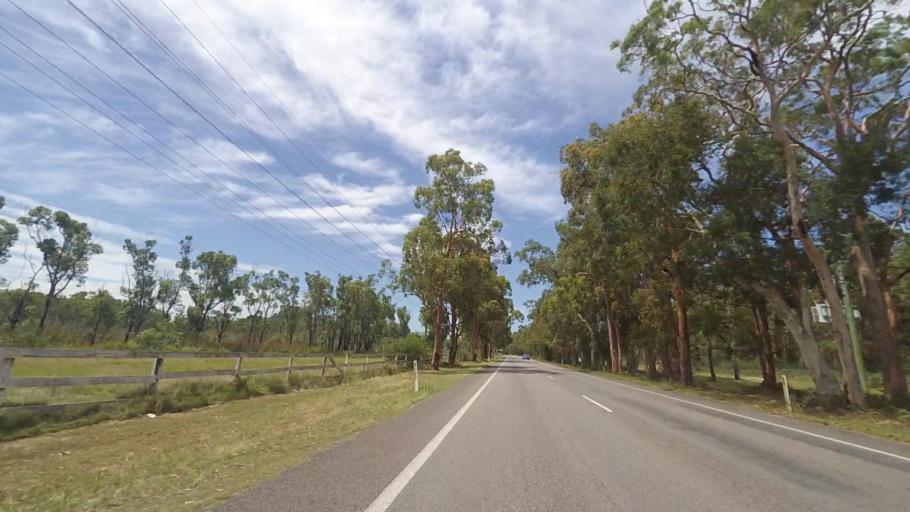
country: AU
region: New South Wales
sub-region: Port Stephens Shire
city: Medowie
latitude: -32.7685
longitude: 151.8624
